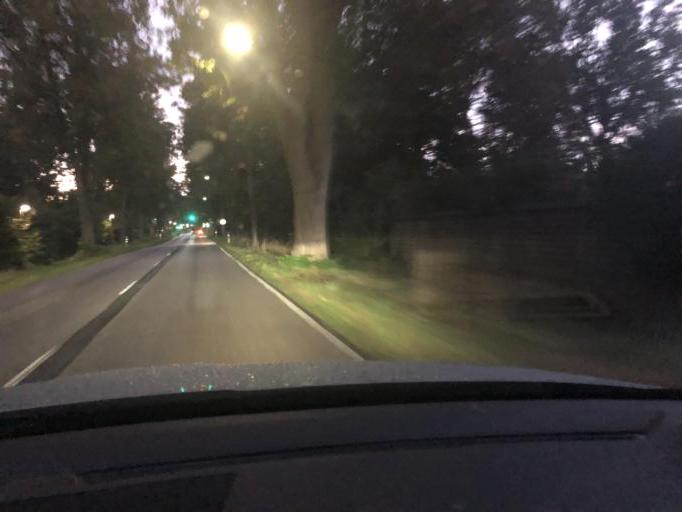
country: DE
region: Schleswig-Holstein
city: Gross Gronau
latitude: 53.8198
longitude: 10.7282
